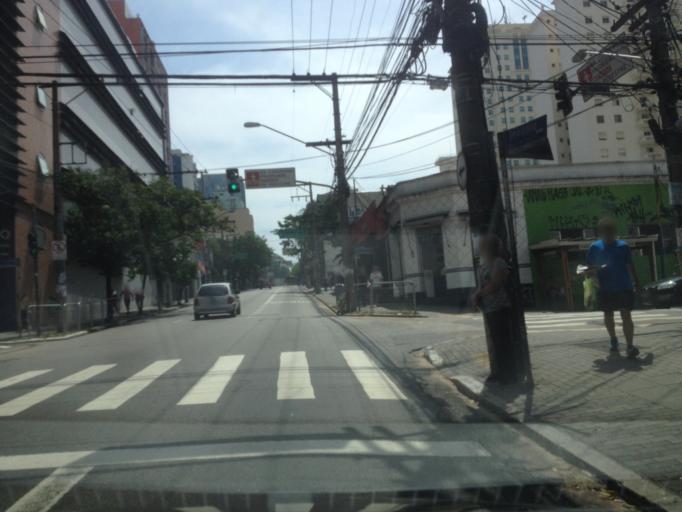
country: BR
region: Sao Paulo
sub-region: Sao Paulo
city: Sao Paulo
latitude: -23.5575
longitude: -46.6773
